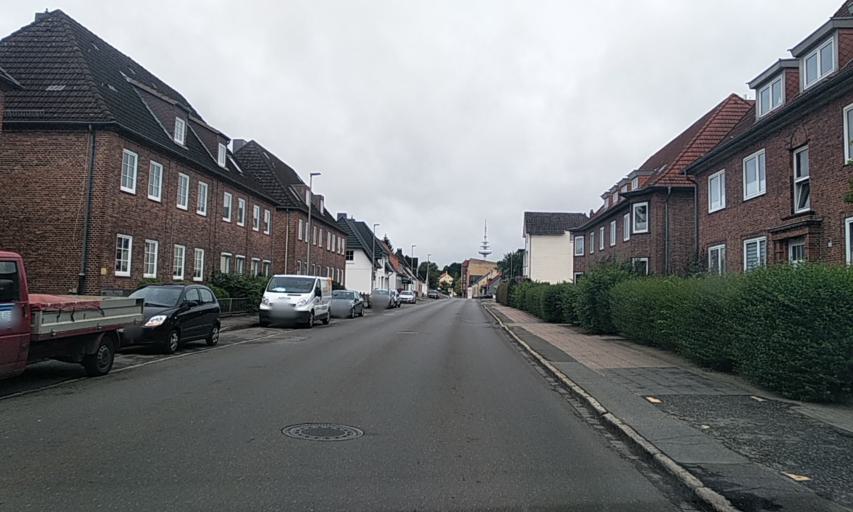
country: DE
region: Schleswig-Holstein
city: Schleswig
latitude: 54.5224
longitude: 9.5482
